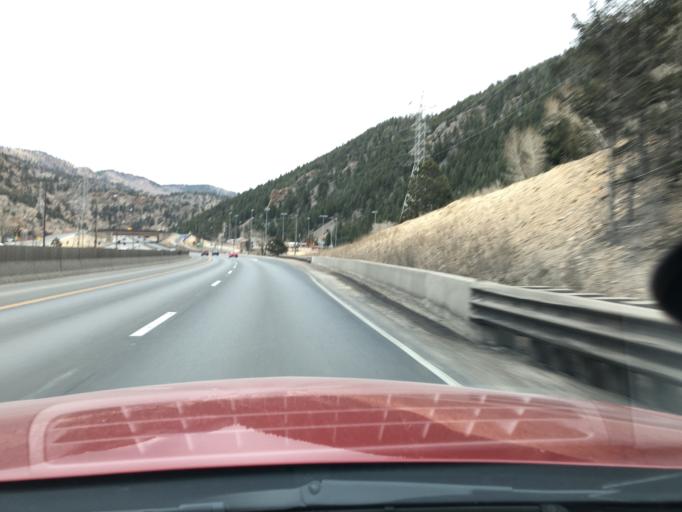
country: US
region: Colorado
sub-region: Clear Creek County
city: Idaho Springs
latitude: 39.7404
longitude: -105.4986
